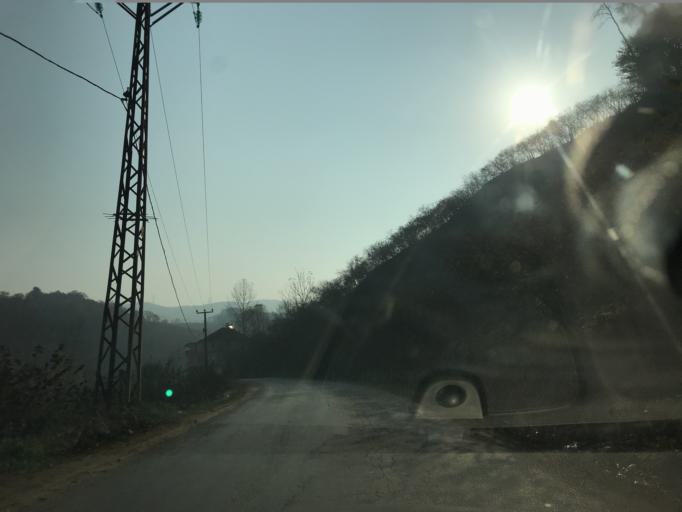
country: TR
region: Duzce
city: Cumayeri
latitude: 40.9084
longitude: 30.9469
